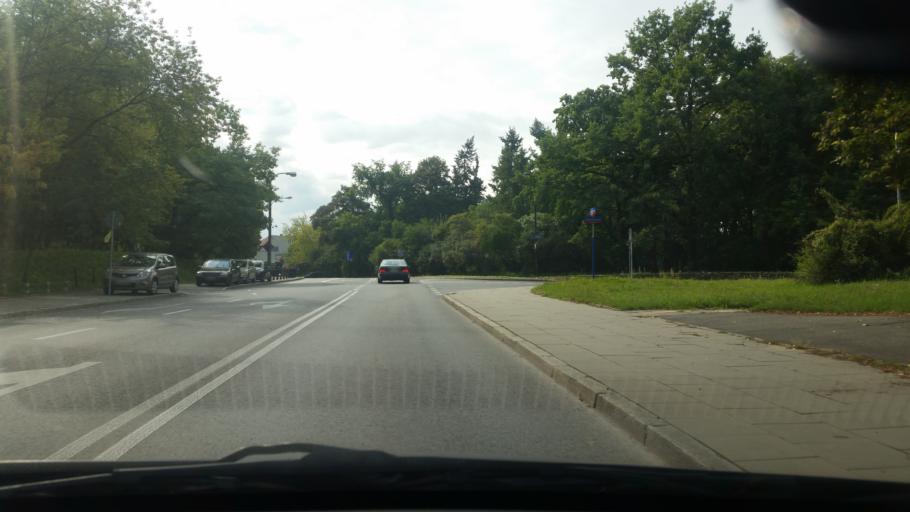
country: PL
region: Masovian Voivodeship
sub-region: Warszawa
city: Zoliborz
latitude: 52.2577
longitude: 21.0043
